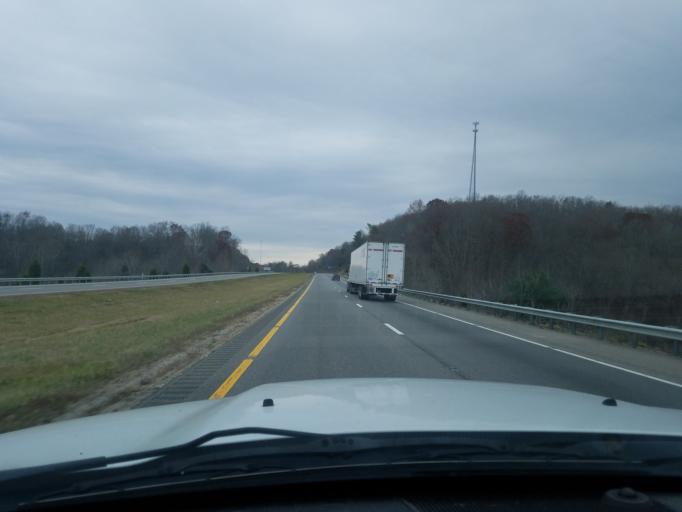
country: US
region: Kentucky
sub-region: Boyd County
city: Meads
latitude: 38.3751
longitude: -82.6770
